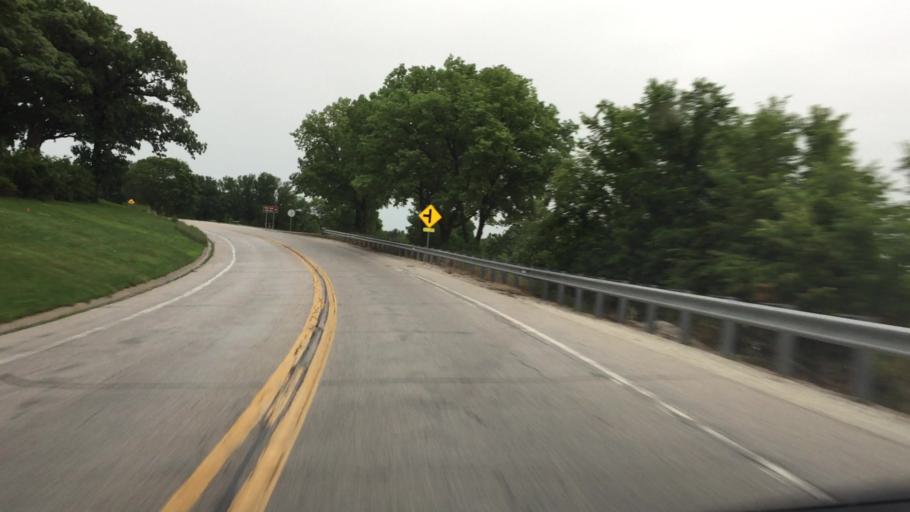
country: US
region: Illinois
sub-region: Hancock County
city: Nauvoo
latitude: 40.5206
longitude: -91.3645
